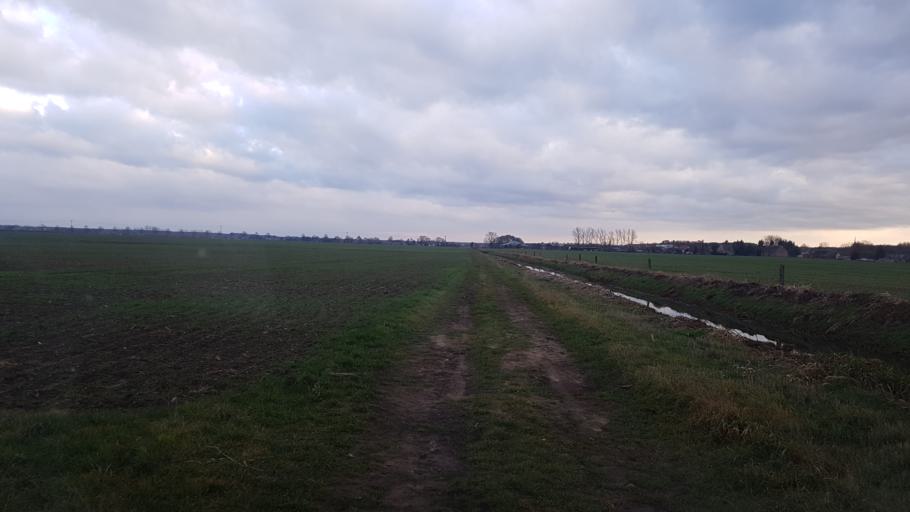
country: DE
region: Brandenburg
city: Schonborn
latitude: 51.5754
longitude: 13.5149
